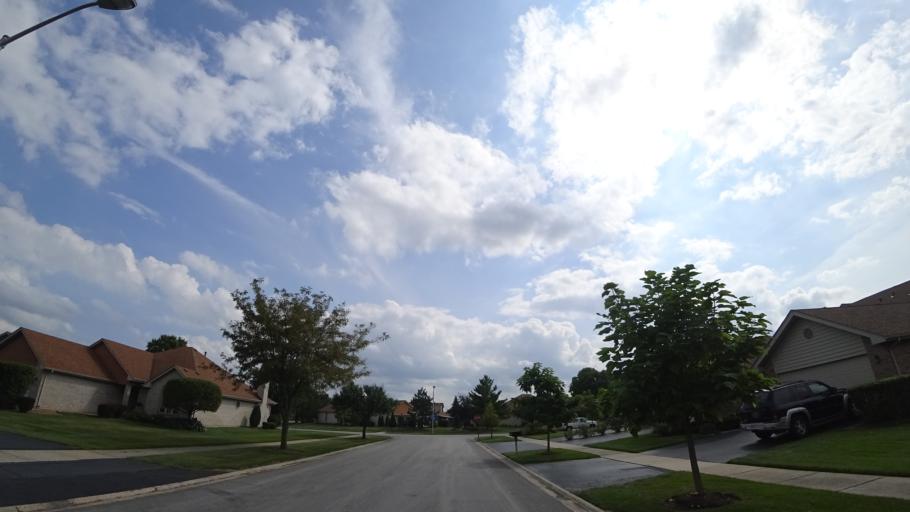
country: US
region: Illinois
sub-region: Cook County
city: Tinley Park
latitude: 41.5583
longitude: -87.7760
